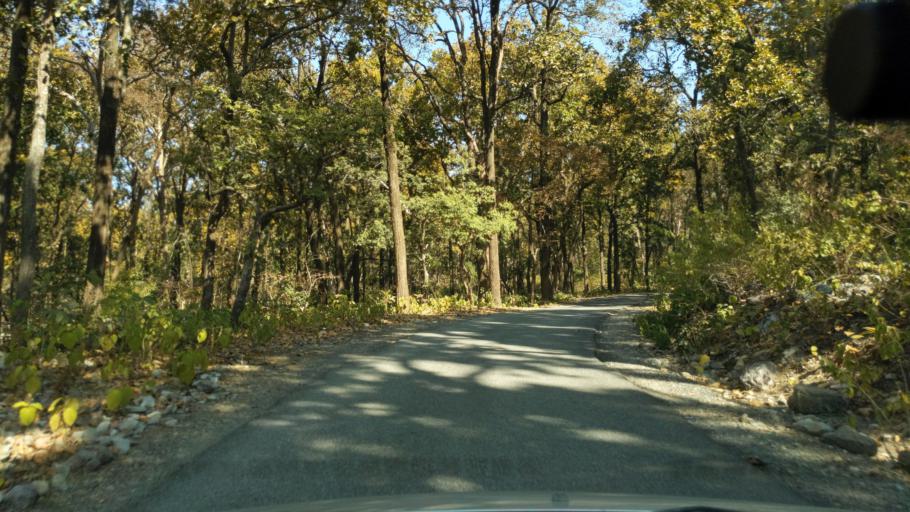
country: IN
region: Uttarakhand
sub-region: Naini Tal
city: Ramnagar
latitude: 29.4630
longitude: 79.2318
